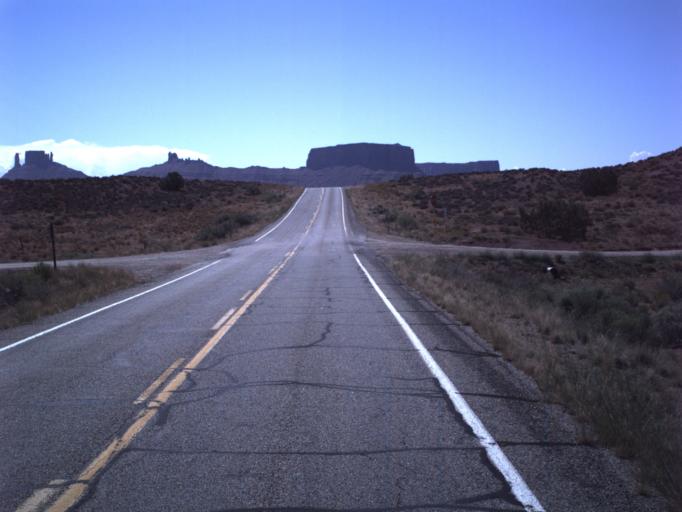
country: US
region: Utah
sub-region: Grand County
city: Moab
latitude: 38.7327
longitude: -109.3450
